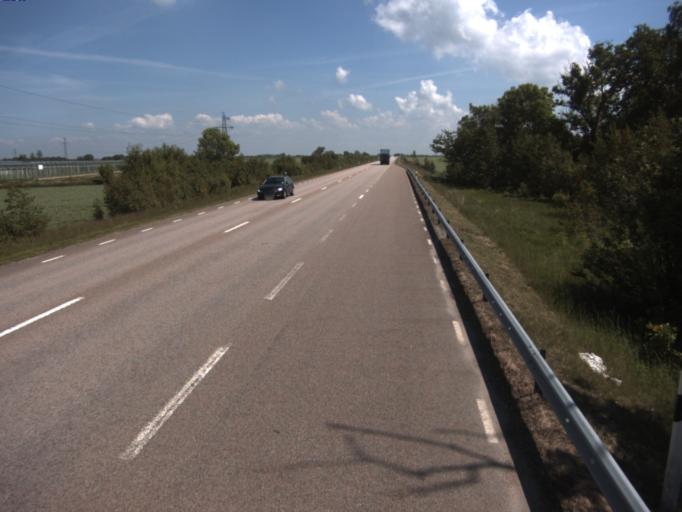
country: SE
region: Skane
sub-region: Helsingborg
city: Barslov
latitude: 56.0136
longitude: 12.8128
